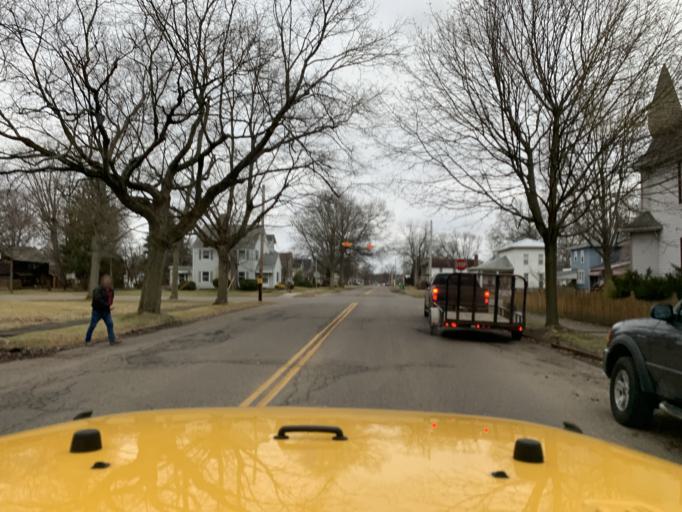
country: US
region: Ohio
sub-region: Tuscarawas County
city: Dover
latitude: 40.5269
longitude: -81.4714
